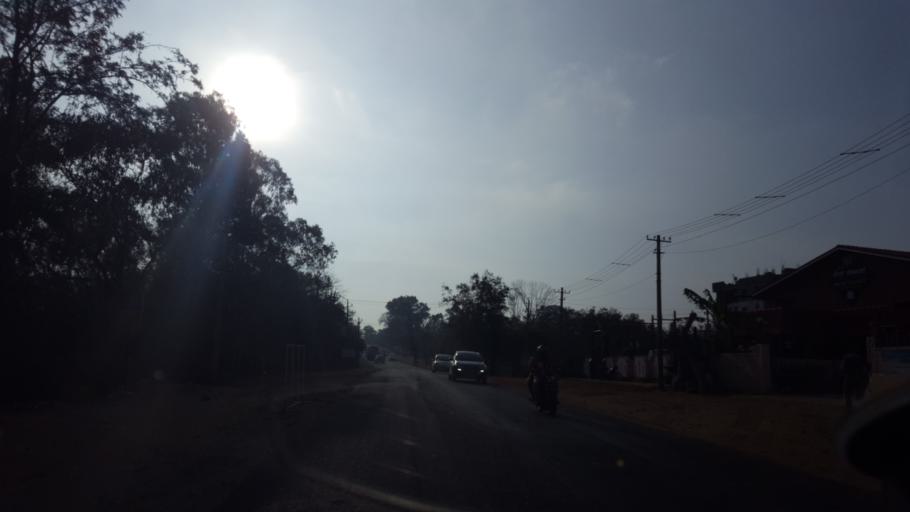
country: IN
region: Karnataka
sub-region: Bangalore Urban
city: Bangalore
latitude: 12.9069
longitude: 77.4997
